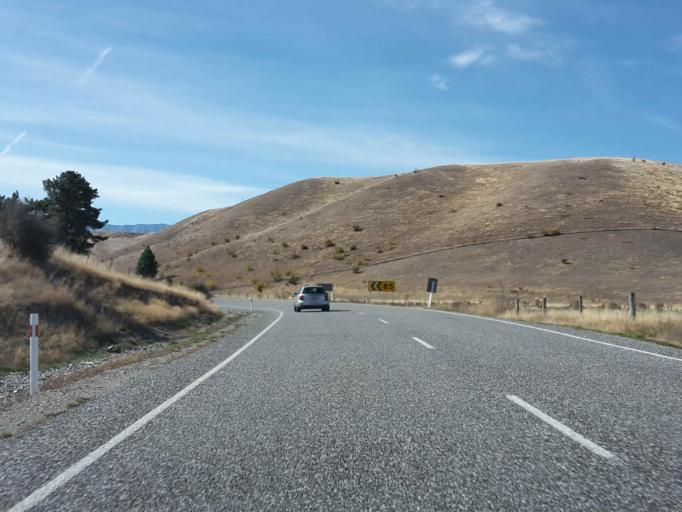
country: NZ
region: Otago
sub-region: Queenstown-Lakes District
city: Wanaka
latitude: -44.8048
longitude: 169.4654
